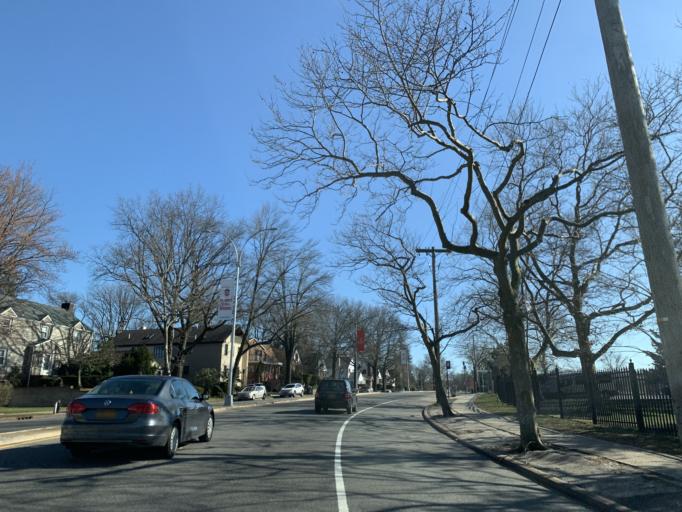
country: US
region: New York
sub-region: Queens County
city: Jamaica
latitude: 40.7238
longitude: -73.7906
